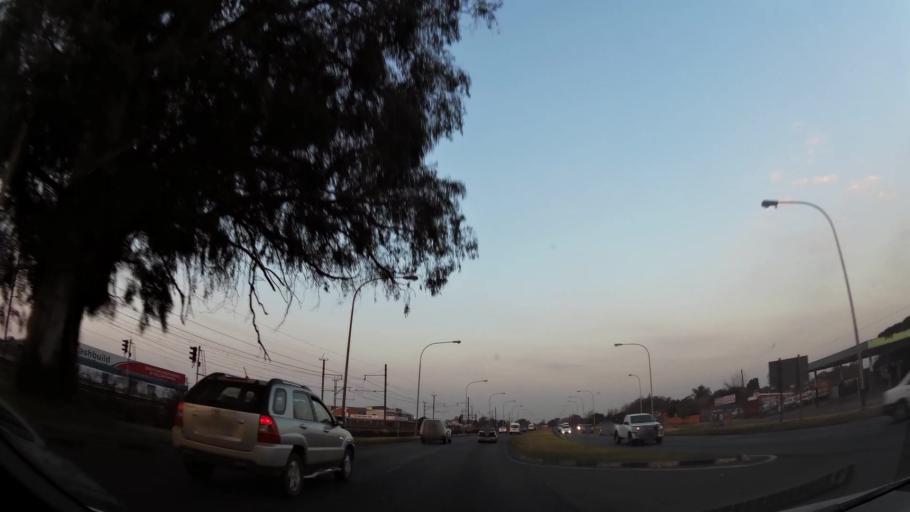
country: ZA
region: Gauteng
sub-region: Ekurhuleni Metropolitan Municipality
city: Springs
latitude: -26.2654
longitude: 28.4209
